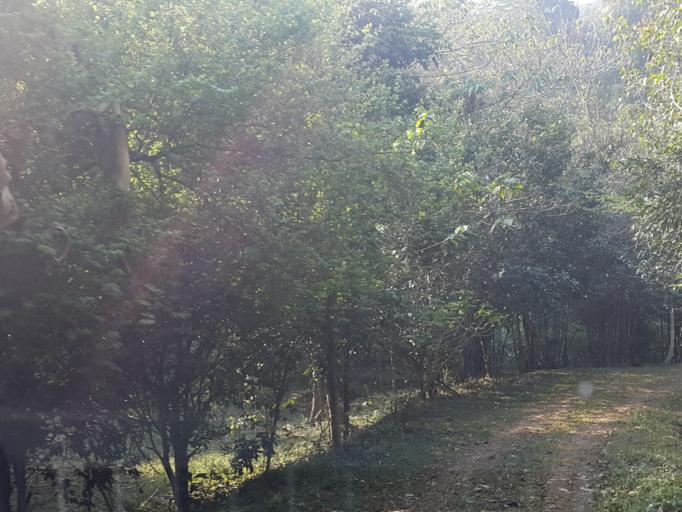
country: TH
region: Chiang Mai
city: Samoeng
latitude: 19.0188
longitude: 98.7553
